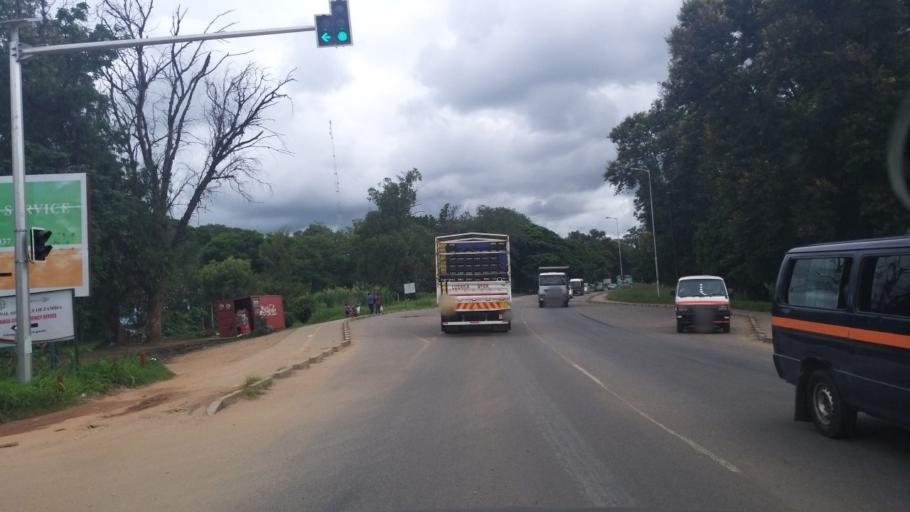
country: ZM
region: Lusaka
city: Lusaka
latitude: -15.5583
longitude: 28.2739
